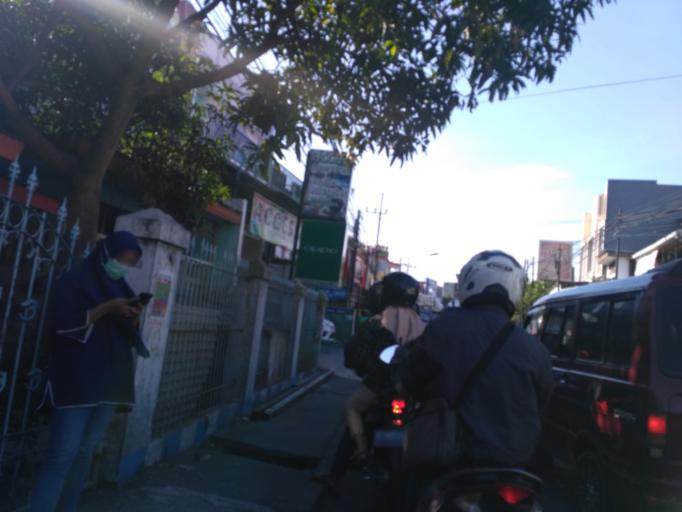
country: ID
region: East Java
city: Malang
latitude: -7.9478
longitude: 112.6087
